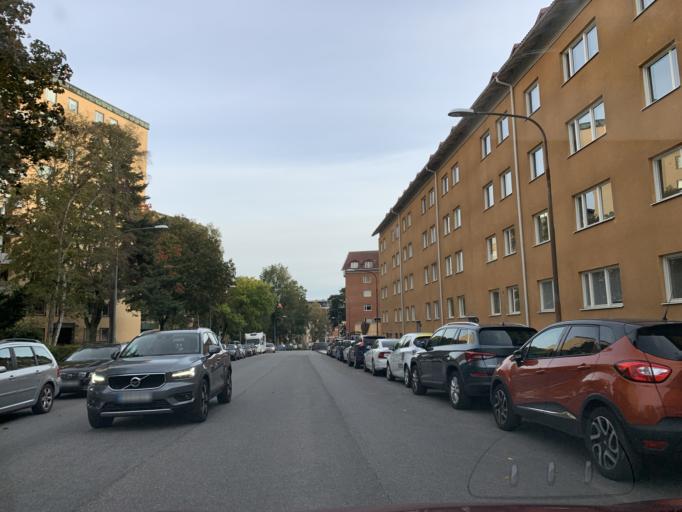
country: SE
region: Stockholm
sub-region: Stockholms Kommun
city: OEstermalm
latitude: 59.3449
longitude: 18.1094
